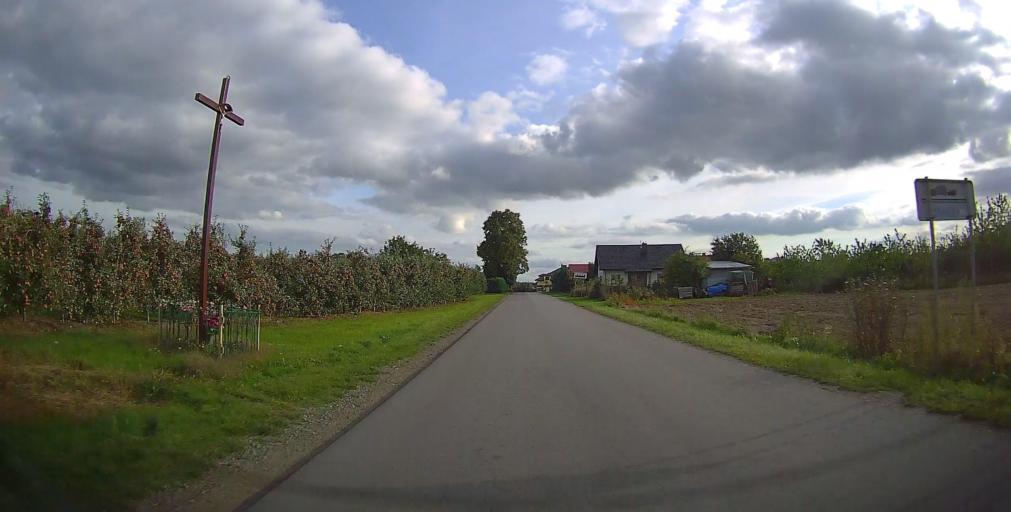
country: PL
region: Masovian Voivodeship
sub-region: Powiat bialobrzeski
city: Promna
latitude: 51.7420
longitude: 20.9650
